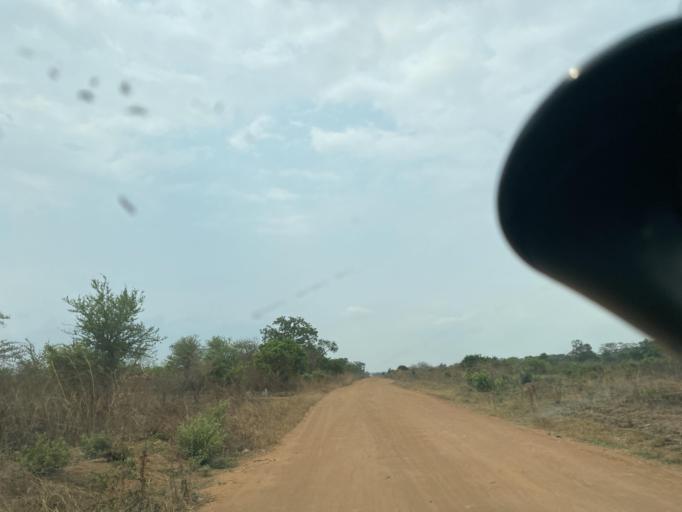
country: ZM
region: Lusaka
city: Lusaka
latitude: -15.2034
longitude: 28.3409
